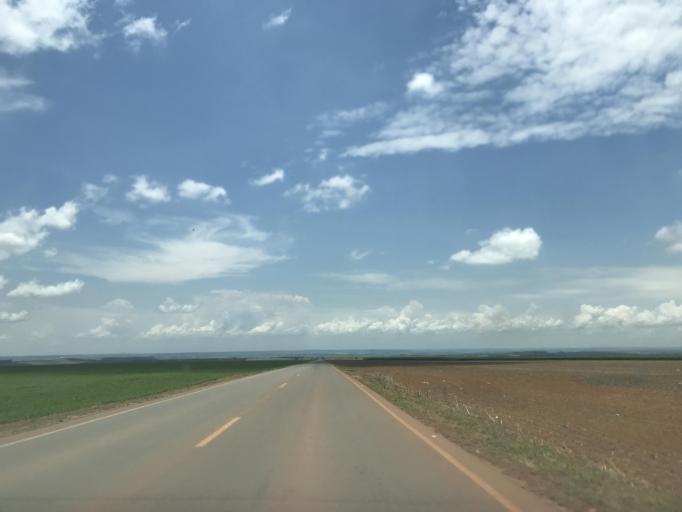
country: BR
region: Goias
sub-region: Vianopolis
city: Vianopolis
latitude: -16.5472
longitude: -48.2663
